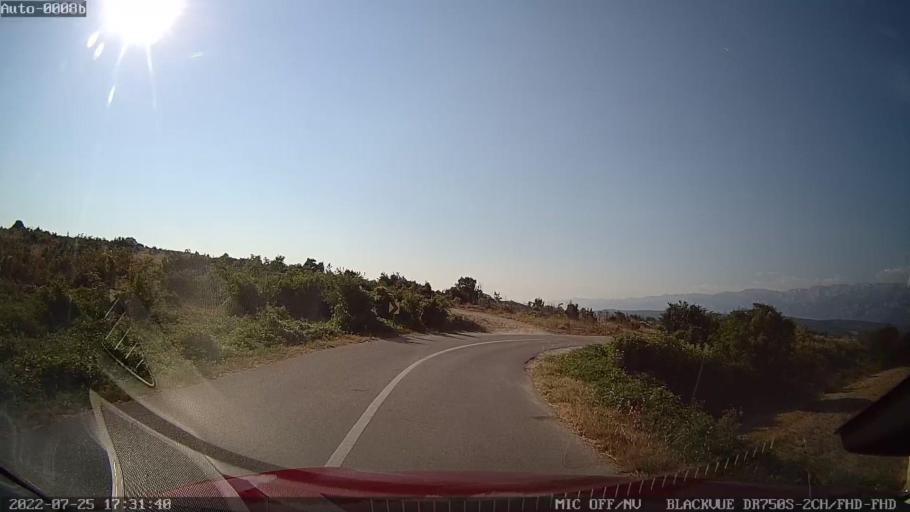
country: HR
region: Zadarska
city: Posedarje
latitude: 44.1718
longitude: 15.4975
